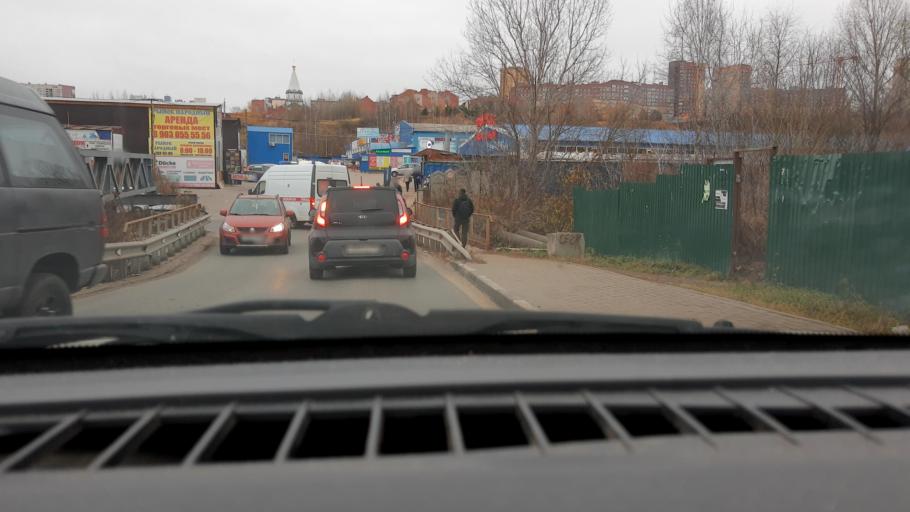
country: RU
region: Nizjnij Novgorod
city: Afonino
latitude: 56.2896
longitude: 44.0558
